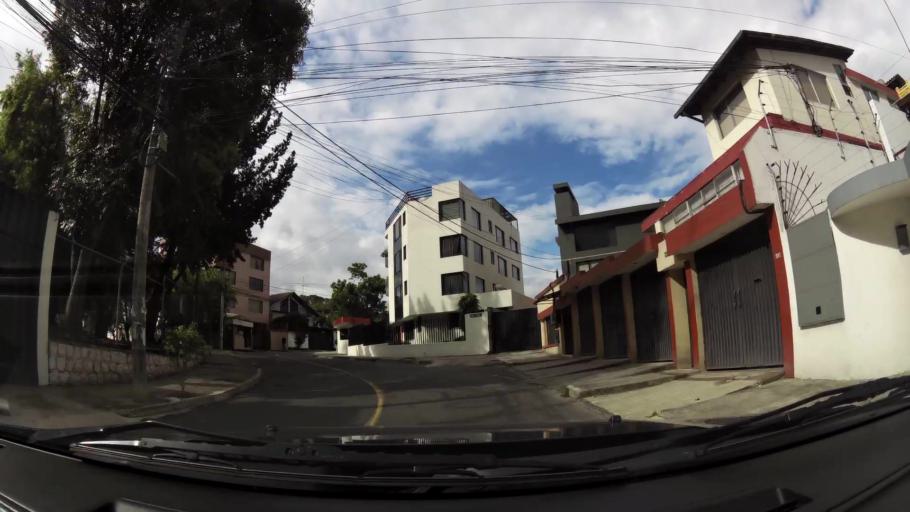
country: EC
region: Pichincha
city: Quito
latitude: -0.1592
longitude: -78.4797
